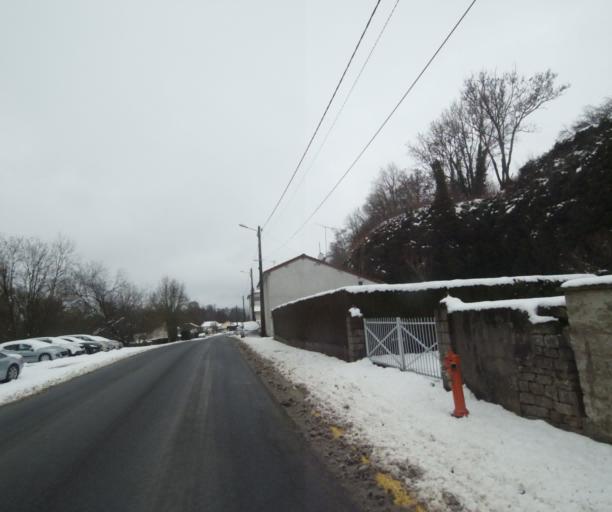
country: FR
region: Champagne-Ardenne
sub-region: Departement de la Haute-Marne
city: Wassy
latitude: 48.4742
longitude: 4.9709
